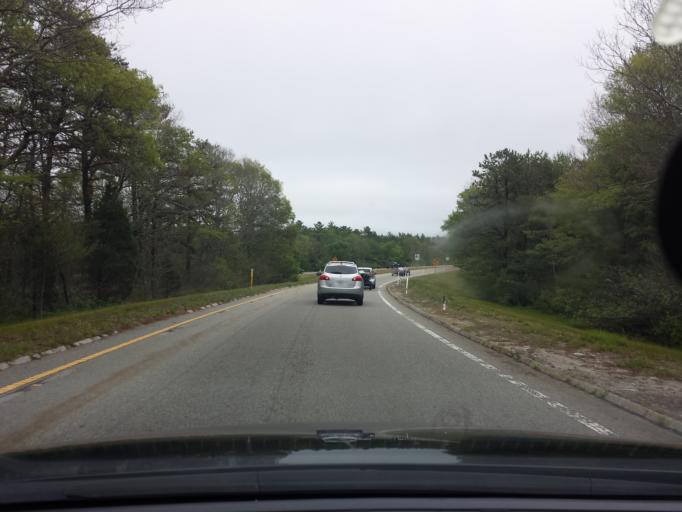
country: US
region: Massachusetts
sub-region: Plymouth County
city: Wareham Center
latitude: 41.7827
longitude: -70.7310
